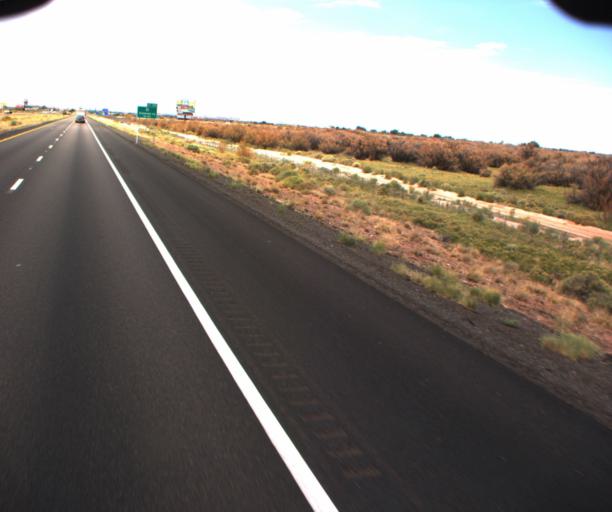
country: US
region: Arizona
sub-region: Navajo County
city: Winslow
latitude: 35.0138
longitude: -110.6590
